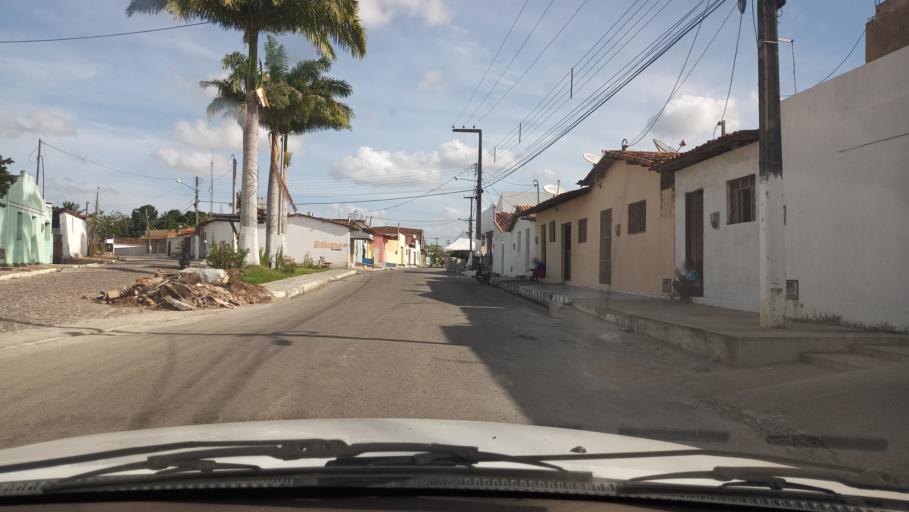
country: BR
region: Rio Grande do Norte
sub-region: Goianinha
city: Goianinha
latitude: -6.3342
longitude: -35.3011
